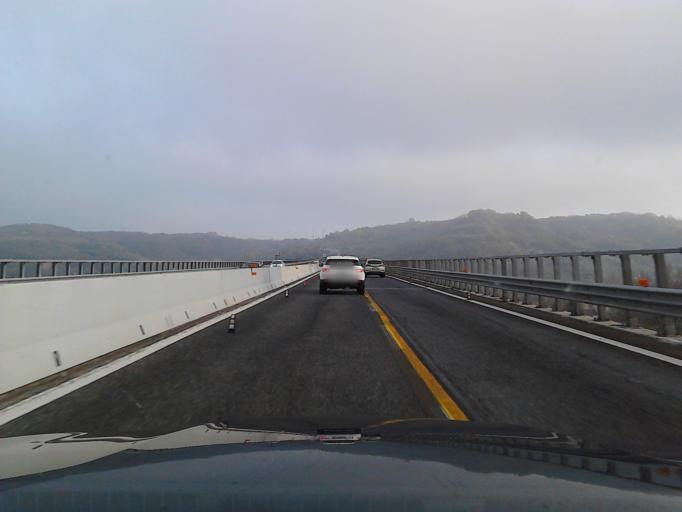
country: IT
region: Abruzzo
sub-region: Provincia di Chieti
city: Miglianico
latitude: 42.3762
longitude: 14.3006
